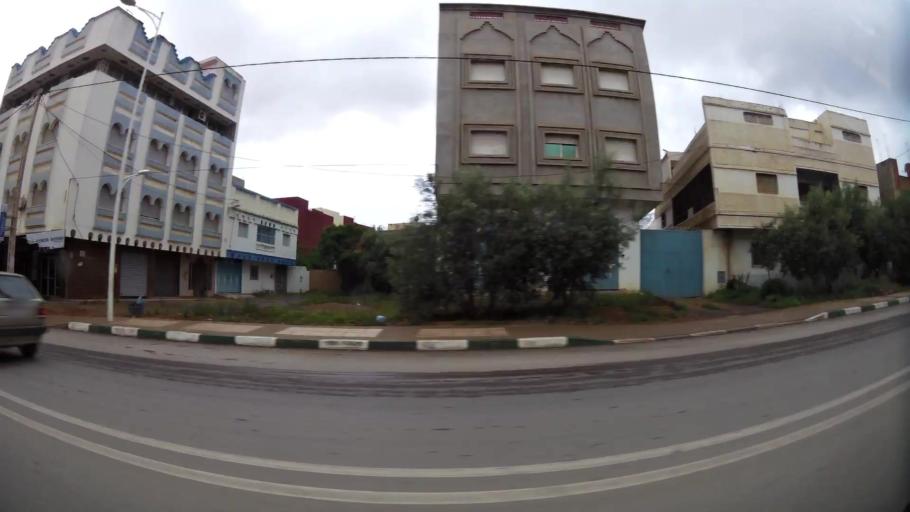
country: MA
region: Oriental
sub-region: Nador
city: Midar
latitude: 35.0495
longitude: -3.4594
